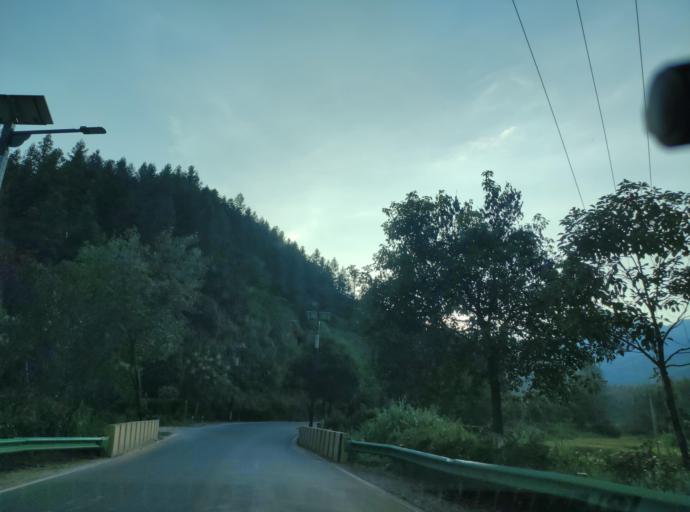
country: CN
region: Jiangxi Sheng
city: Zhangjiafang
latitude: 27.5280
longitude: 114.0274
